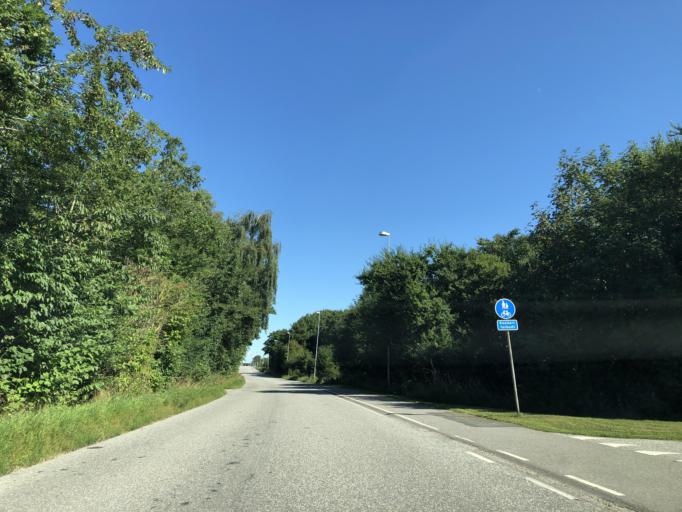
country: DK
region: North Denmark
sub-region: Mariagerfjord Kommune
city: Hobro
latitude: 56.6407
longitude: 9.7747
